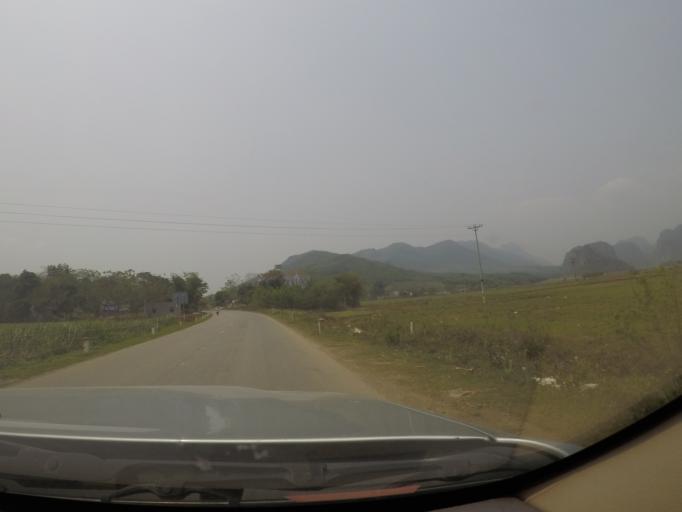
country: VN
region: Thanh Hoa
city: Thi Tran Cam Thuy
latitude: 20.1506
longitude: 105.4437
